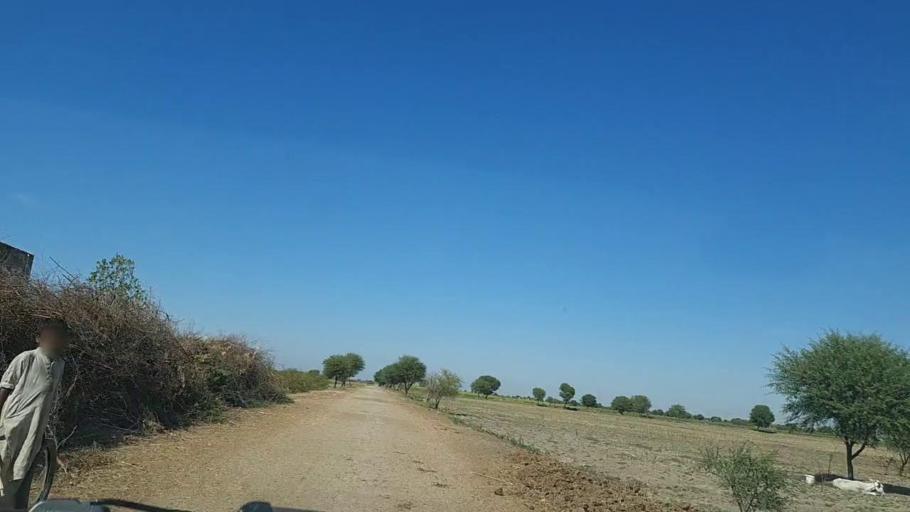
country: PK
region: Sindh
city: Pithoro
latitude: 25.5506
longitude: 69.4599
